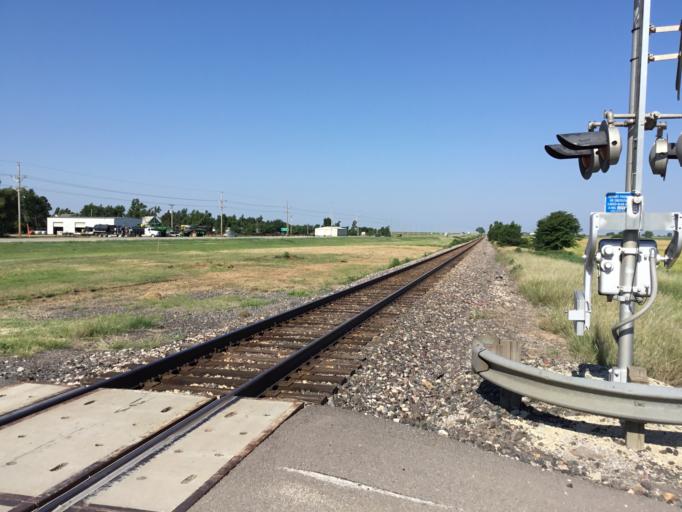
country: US
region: Kansas
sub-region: Pratt County
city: Pratt
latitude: 37.6331
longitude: -98.9049
